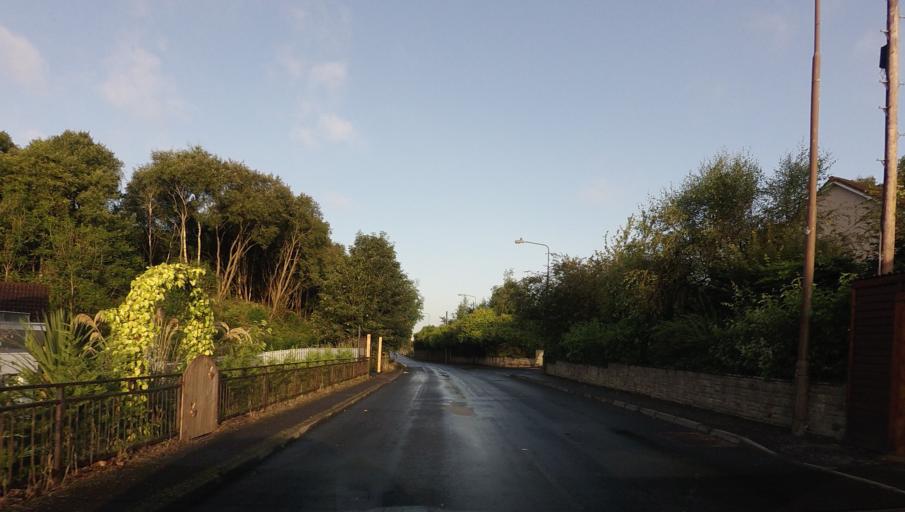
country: GB
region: Scotland
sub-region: West Lothian
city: Bathgate
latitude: 55.9070
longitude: -3.6493
